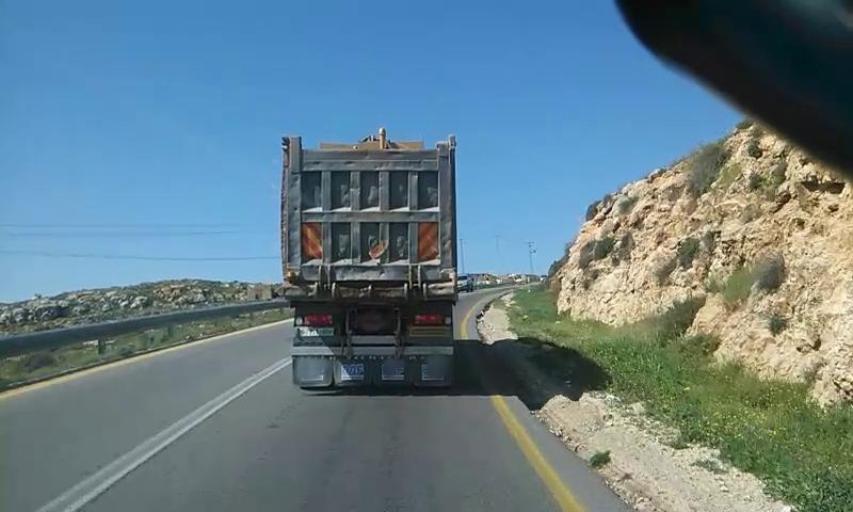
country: PS
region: West Bank
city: Jurat ash Sham`ah
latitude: 31.6475
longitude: 35.1778
